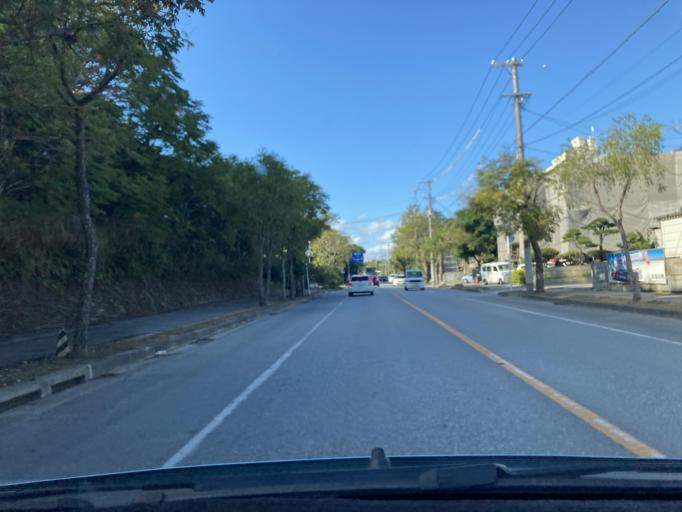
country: JP
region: Okinawa
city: Gushikawa
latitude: 26.3699
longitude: 127.8299
